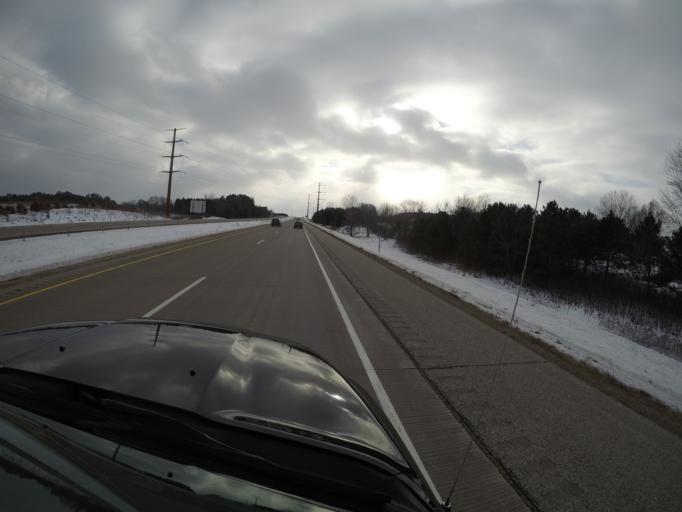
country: US
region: Wisconsin
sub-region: La Crosse County
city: Holmen
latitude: 43.9763
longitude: -91.2864
